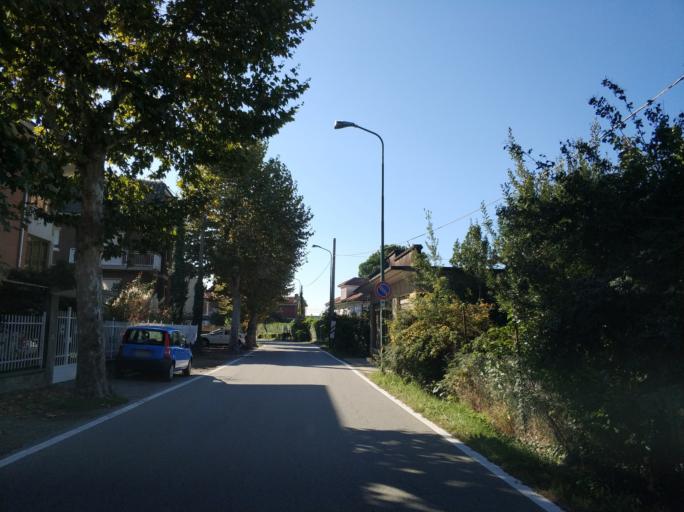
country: IT
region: Piedmont
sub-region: Provincia di Torino
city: Nole
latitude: 45.2445
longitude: 7.5670
